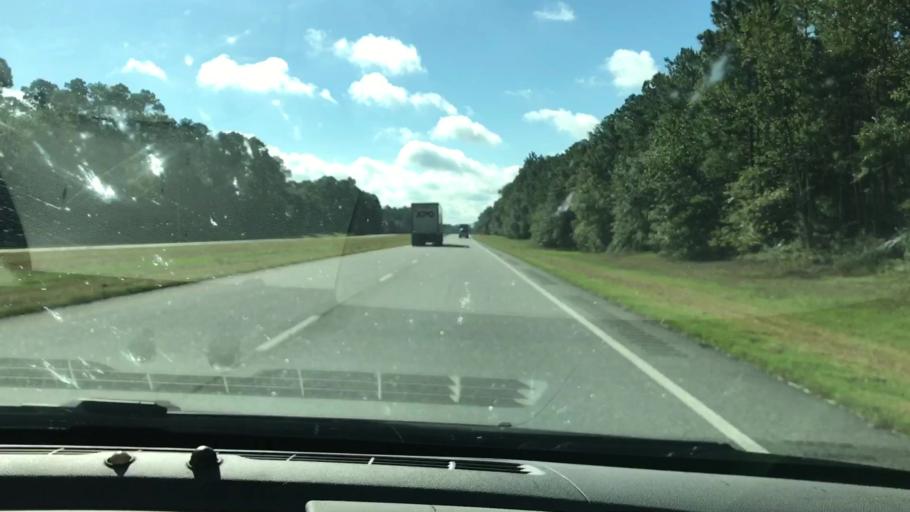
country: US
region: Georgia
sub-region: Dougherty County
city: Putney
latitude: 31.5645
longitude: -84.0157
